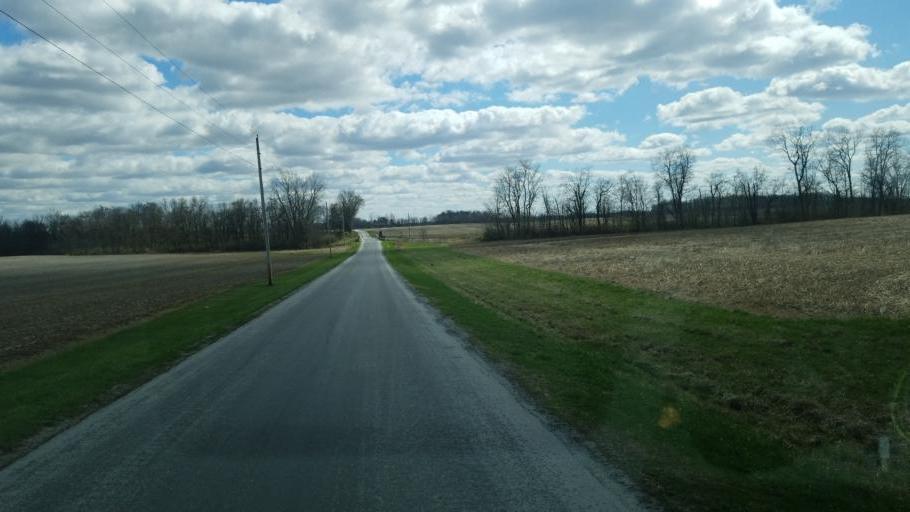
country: US
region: Ohio
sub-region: Hardin County
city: Kenton
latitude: 40.6357
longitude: -83.5619
